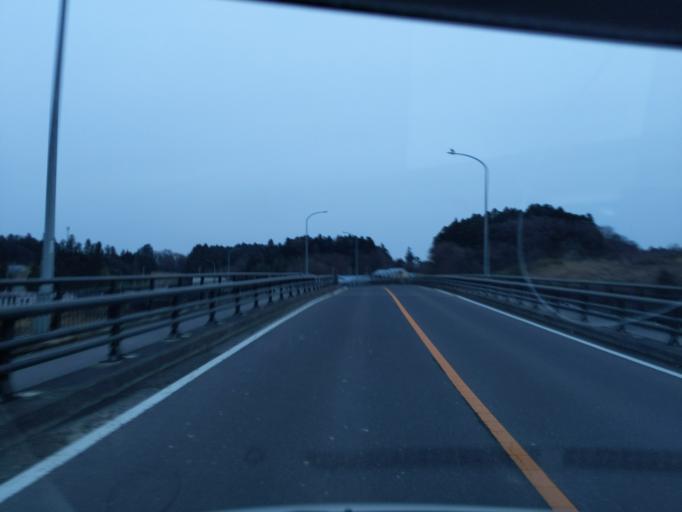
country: JP
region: Miyagi
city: Wakuya
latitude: 38.7079
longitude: 141.1129
